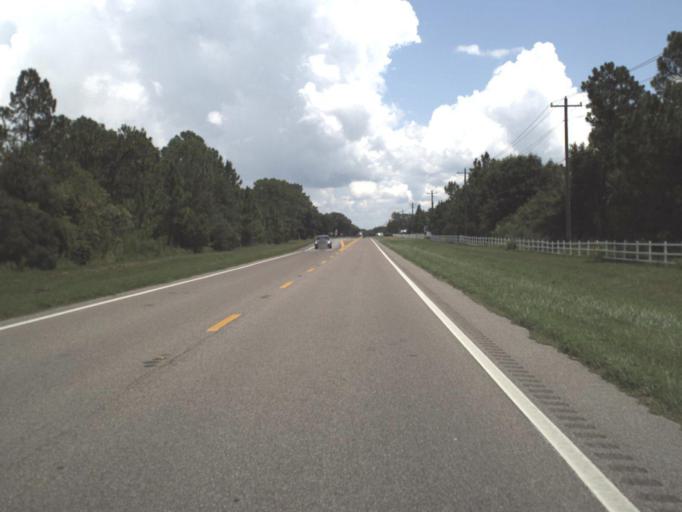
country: US
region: Florida
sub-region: Hillsborough County
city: Sun City Center
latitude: 27.6619
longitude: -82.3649
